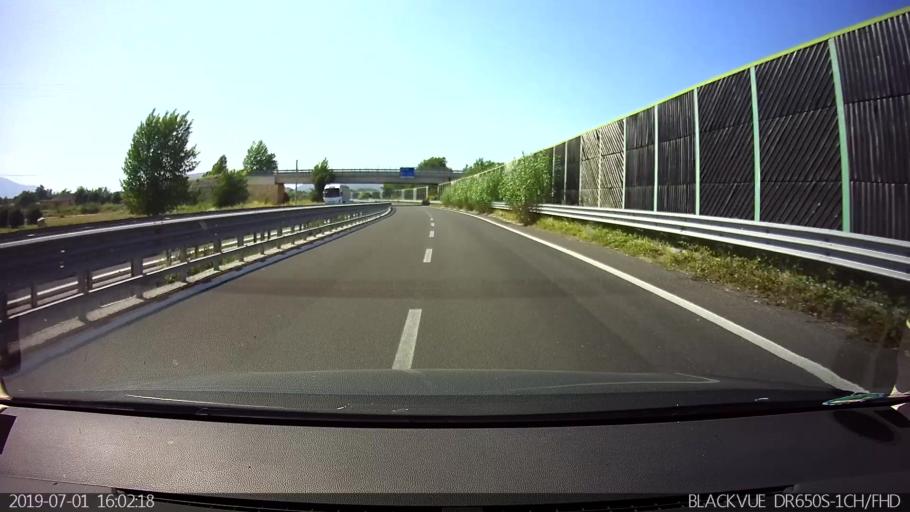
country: IT
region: Latium
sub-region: Provincia di Frosinone
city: Castelmassimo
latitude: 41.6690
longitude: 13.3592
